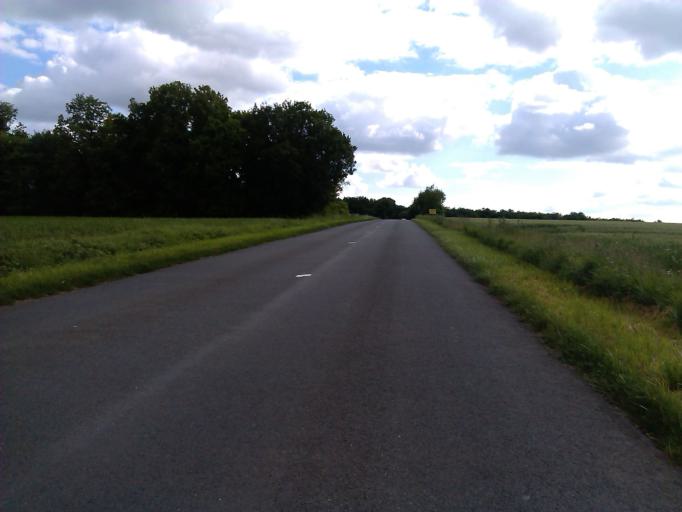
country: FR
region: Poitou-Charentes
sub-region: Departement de la Charente
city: Mansle
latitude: 45.8547
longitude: 0.1630
